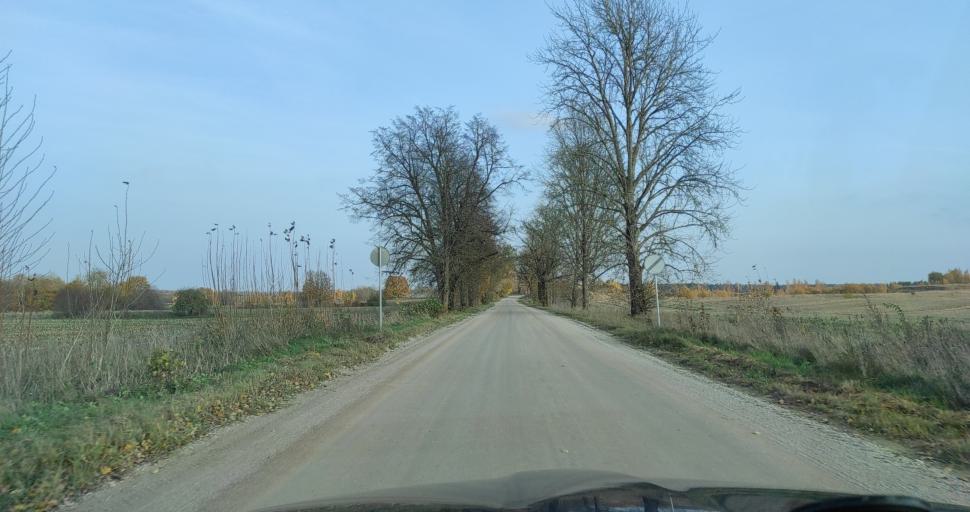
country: LV
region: Vainode
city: Vainode
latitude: 56.4431
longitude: 21.8627
